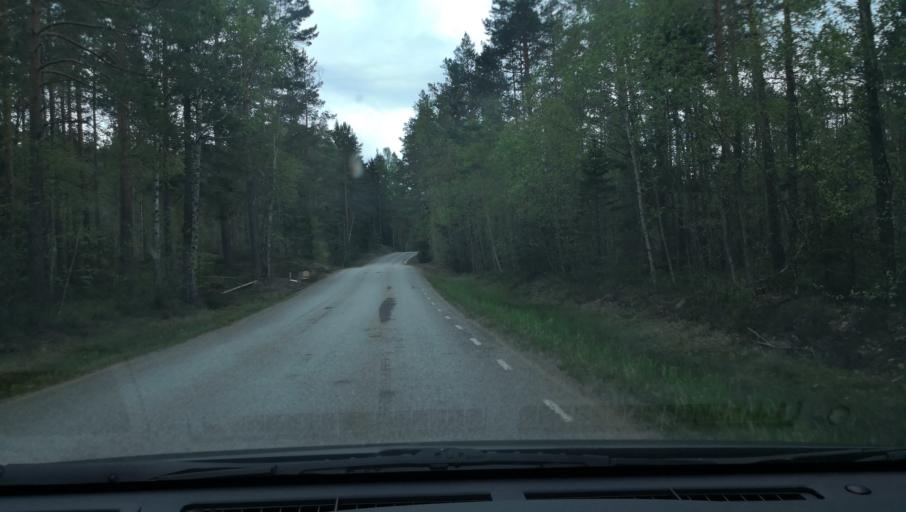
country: SE
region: Vaestmanland
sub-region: Skinnskattebergs Kommun
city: Skinnskatteberg
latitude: 59.8182
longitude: 15.5533
